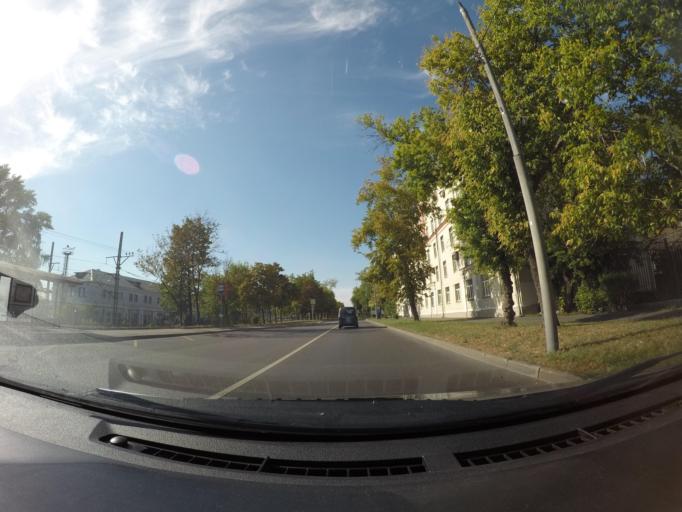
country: RU
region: Moscow
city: Mar'ina Roshcha
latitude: 55.8039
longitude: 37.6275
